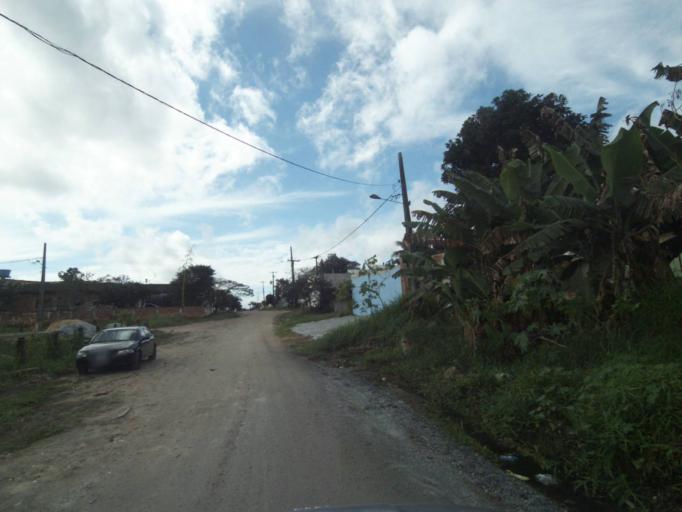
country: BR
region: Parana
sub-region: Paranagua
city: Paranagua
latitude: -25.5698
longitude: -48.5647
